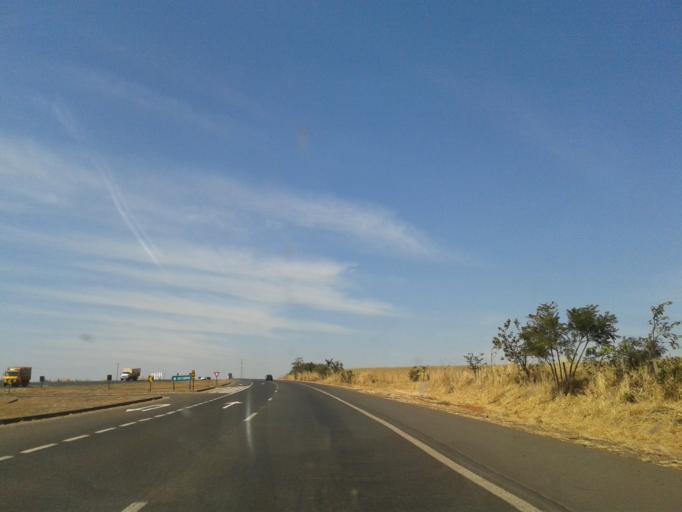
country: BR
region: Minas Gerais
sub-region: Monte Alegre De Minas
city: Monte Alegre de Minas
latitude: -18.8561
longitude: -49.0796
